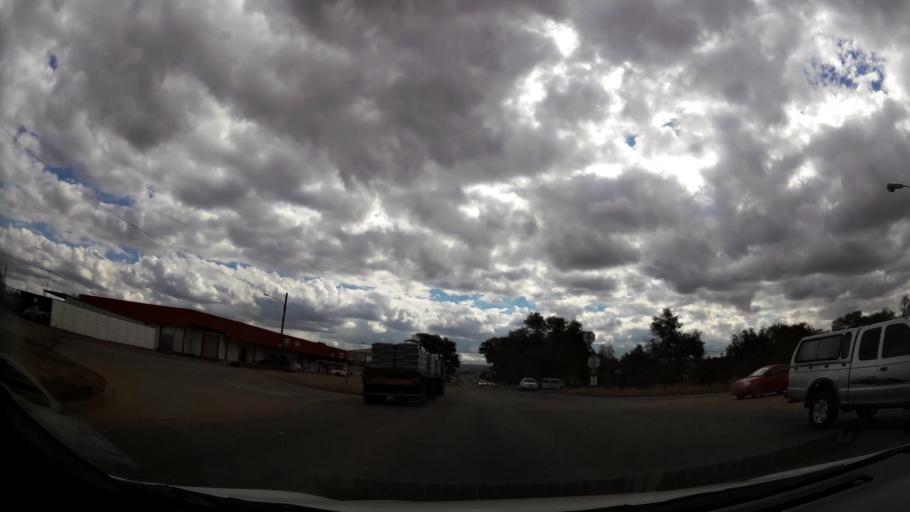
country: ZA
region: Limpopo
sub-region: Waterberg District Municipality
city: Modimolle
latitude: -24.7165
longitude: 28.4204
